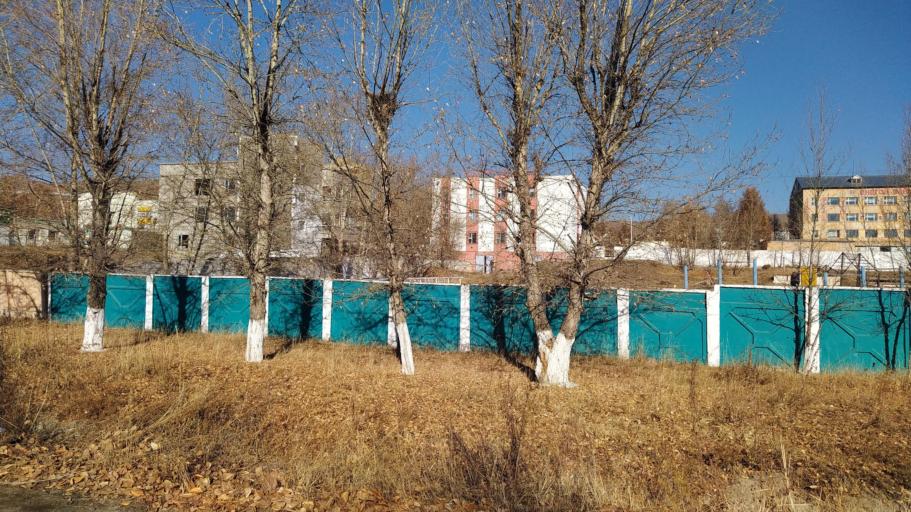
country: MN
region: Orhon
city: Erdenet
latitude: 49.0331
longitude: 104.0757
